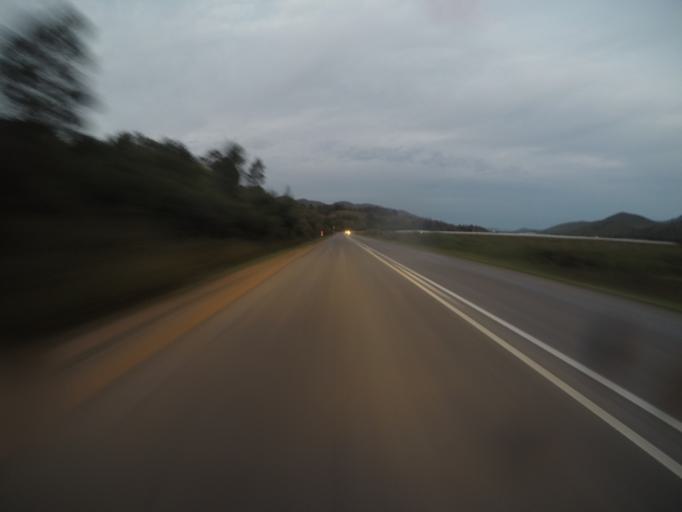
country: ZA
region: Western Cape
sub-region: Eden District Municipality
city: Plettenberg Bay
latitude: -33.8112
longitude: 23.7433
